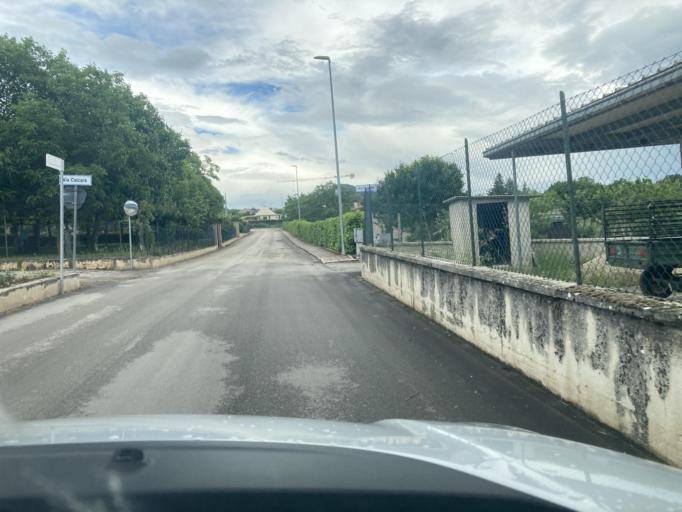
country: IT
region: Abruzzo
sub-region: Provincia dell' Aquila
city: San Demetrio Ne' Vestini
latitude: 42.2933
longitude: 13.5556
